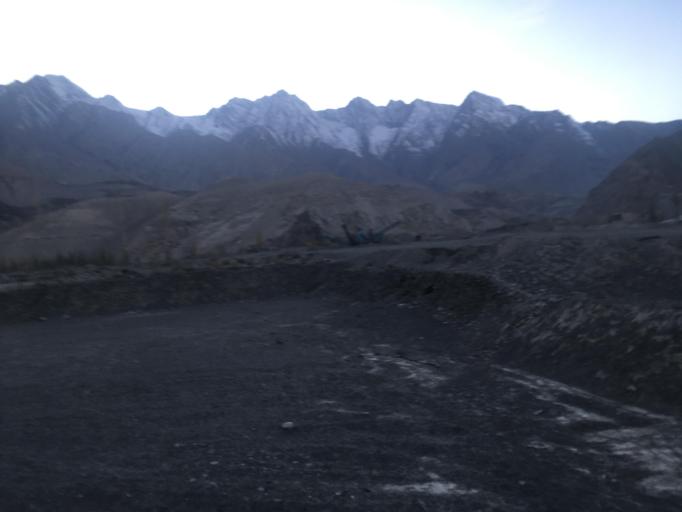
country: PK
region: Gilgit-Baltistan
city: Skardu
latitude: 35.3061
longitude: 75.5388
